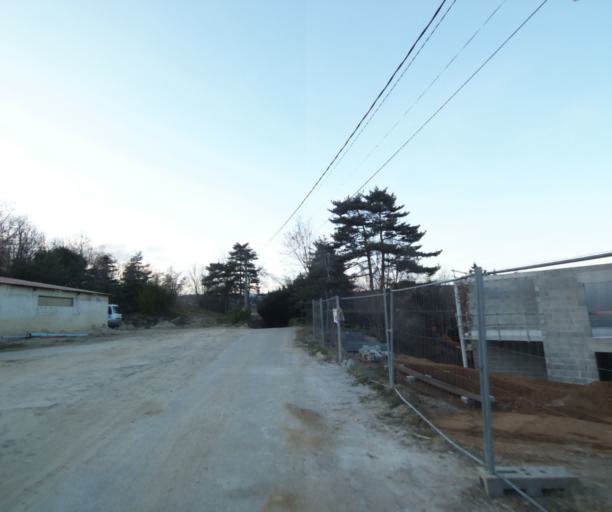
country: FR
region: Rhone-Alpes
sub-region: Departement de l'Ardeche
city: Davezieux
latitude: 45.2587
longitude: 4.7111
